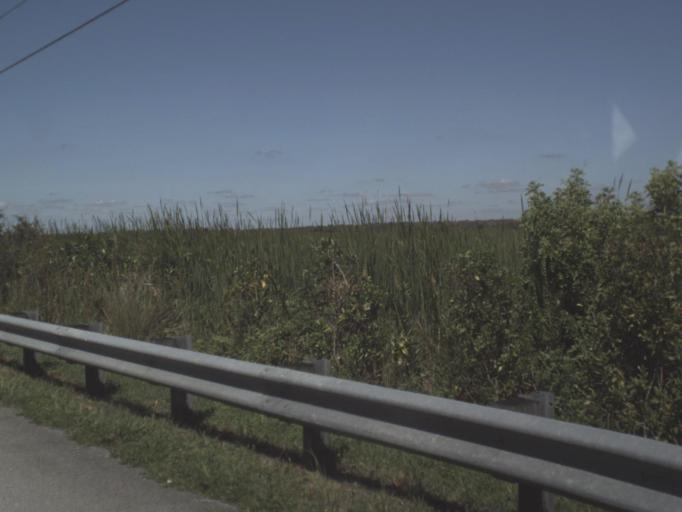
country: US
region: Florida
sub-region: Collier County
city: Marco
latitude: 25.9191
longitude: -81.3986
